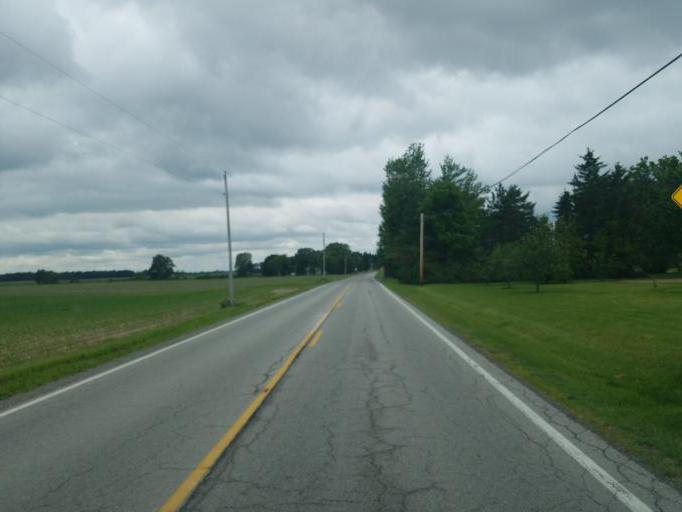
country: US
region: Ohio
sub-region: Crawford County
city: Bucyrus
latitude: 40.7707
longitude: -82.9261
